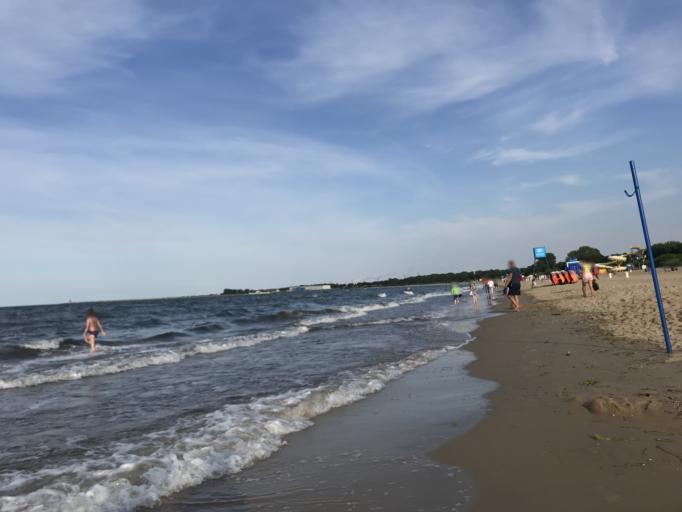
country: PL
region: Pomeranian Voivodeship
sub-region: Gdansk
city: Gdansk
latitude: 54.4135
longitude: 18.6260
